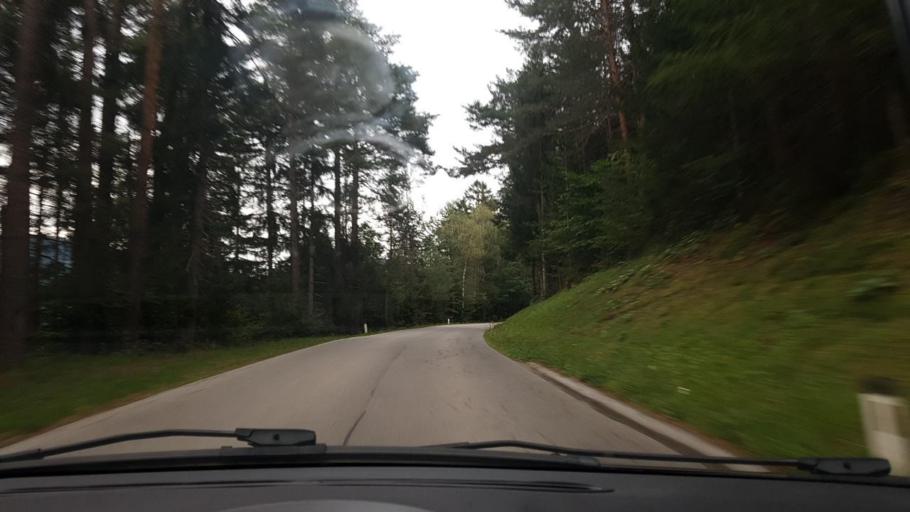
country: AT
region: Tyrol
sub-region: Politischer Bezirk Lienz
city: Amlach
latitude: 46.8125
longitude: 12.7743
